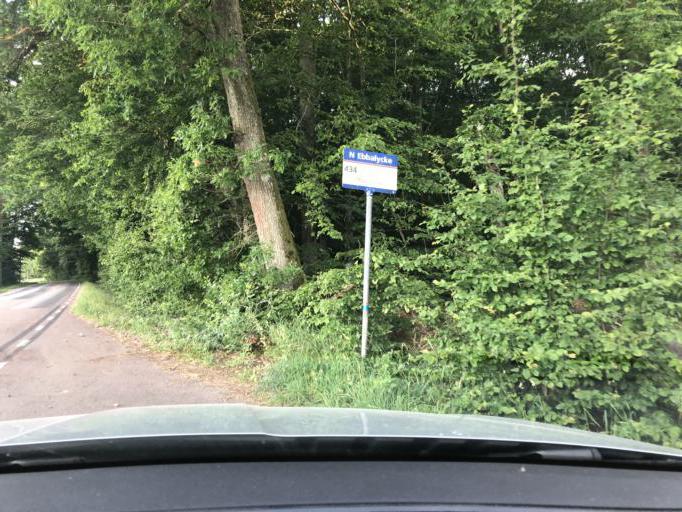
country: SE
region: Blekinge
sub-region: Solvesborgs Kommun
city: Soelvesborg
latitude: 56.1399
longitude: 14.6067
